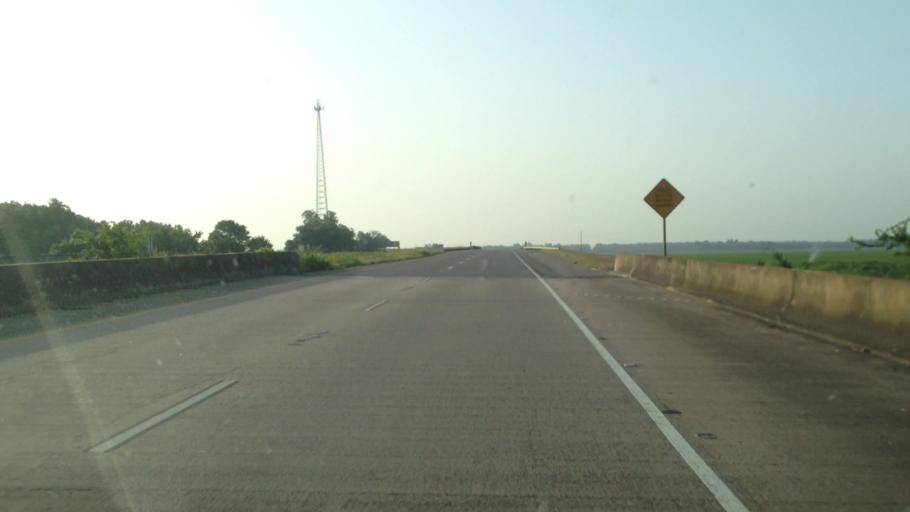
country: US
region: Louisiana
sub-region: Rapides Parish
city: Boyce
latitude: 31.3939
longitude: -92.6952
